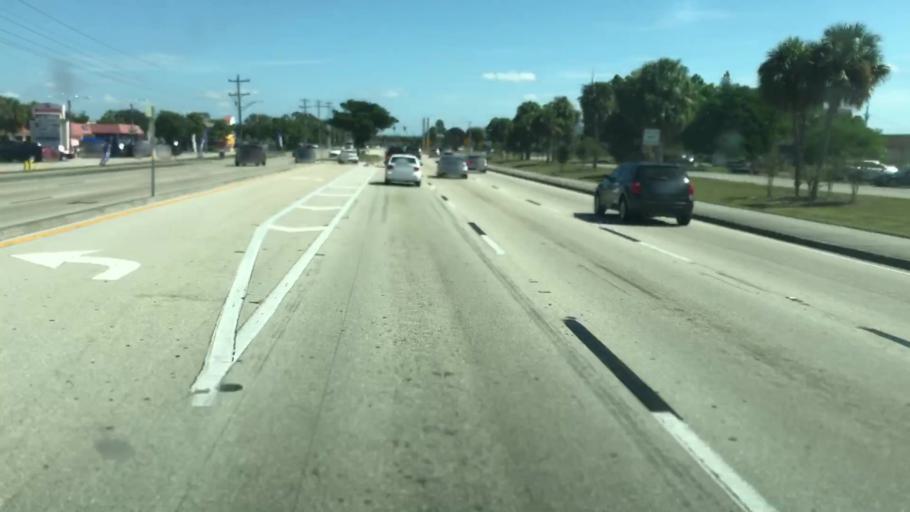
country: US
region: Florida
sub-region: Lee County
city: Lehigh Acres
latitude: 26.6142
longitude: -81.6570
